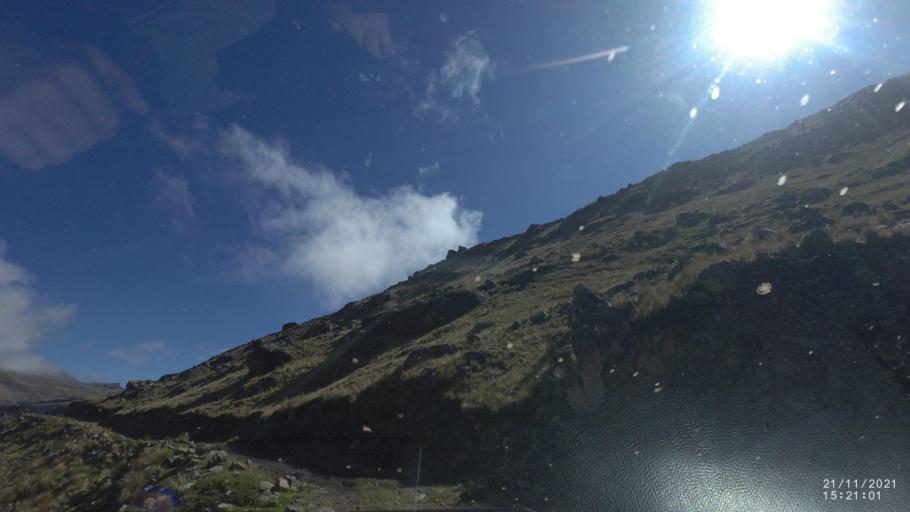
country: BO
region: Cochabamba
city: Cochabamba
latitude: -16.9579
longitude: -66.2669
